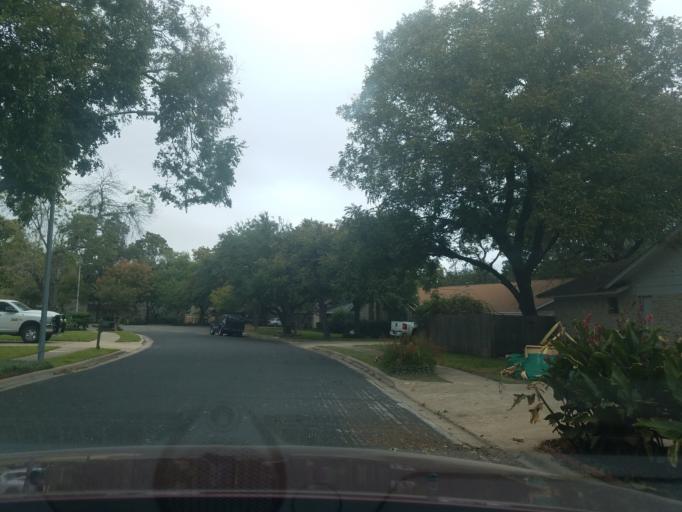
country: US
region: Texas
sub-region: Williamson County
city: Anderson Mill
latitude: 30.4592
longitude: -97.8037
